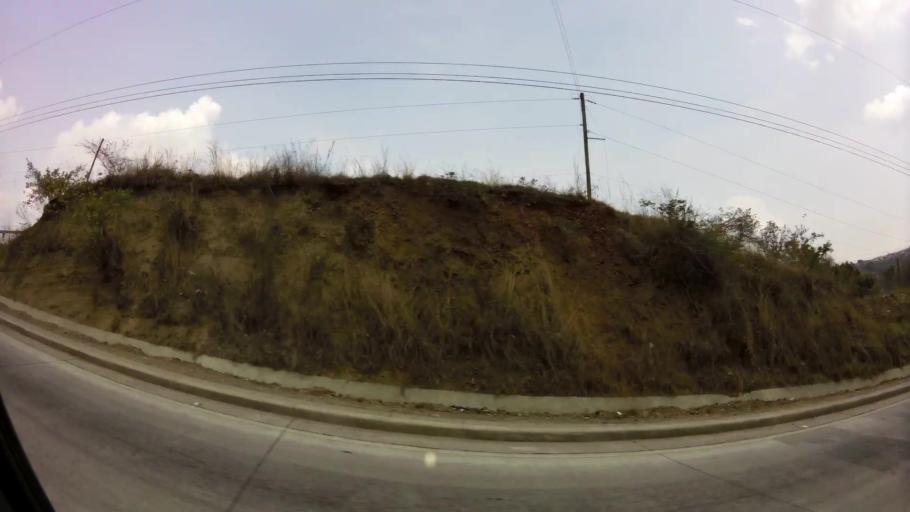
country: HN
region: Francisco Morazan
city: El Lolo
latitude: 14.0896
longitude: -87.2462
